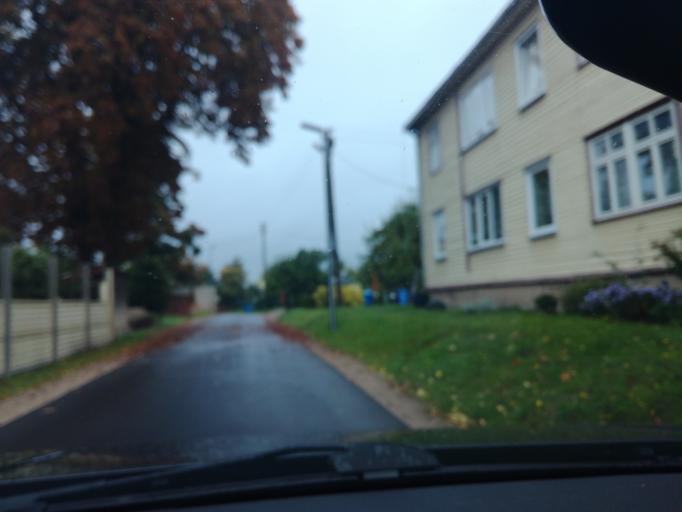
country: LT
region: Alytaus apskritis
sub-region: Alytus
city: Alytus
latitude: 54.3999
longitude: 24.0704
